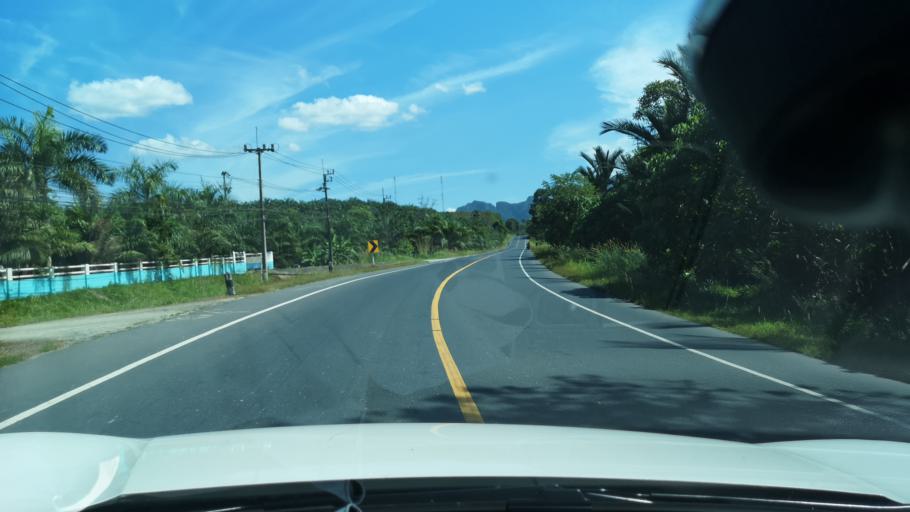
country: TH
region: Phangnga
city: Phang Nga
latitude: 8.5392
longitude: 98.4961
